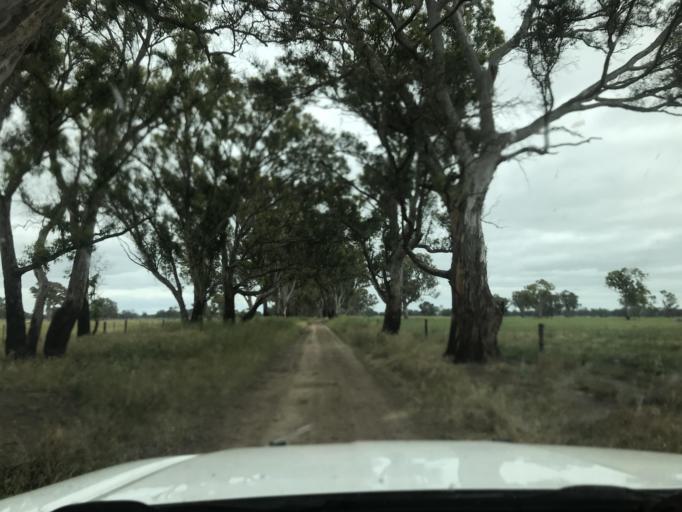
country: AU
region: South Australia
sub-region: Wattle Range
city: Penola
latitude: -37.1788
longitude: 141.0583
